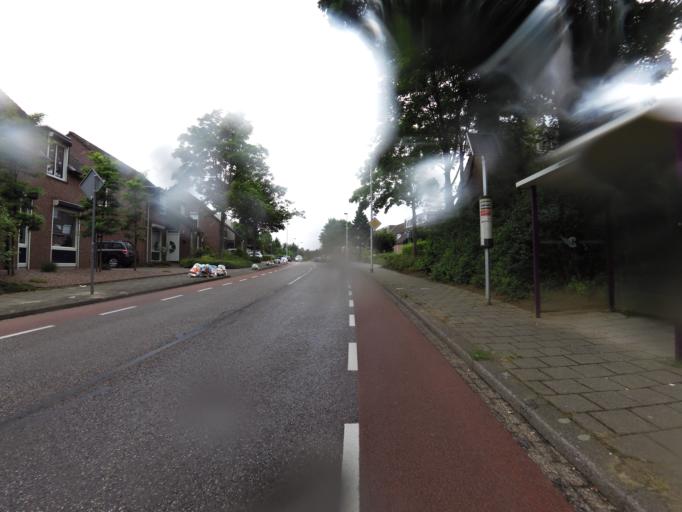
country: NL
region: Limburg
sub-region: Gemeente Heerlen
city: Heerlen
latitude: 50.8730
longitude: 6.0065
